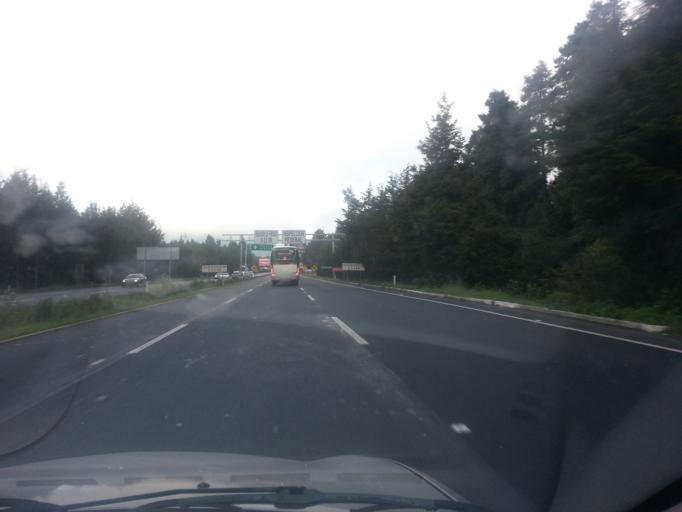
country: MX
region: Mexico City
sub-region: Cuajimalpa de Morelos
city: San Lorenzo Acopilco
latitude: 19.2999
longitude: -99.3638
